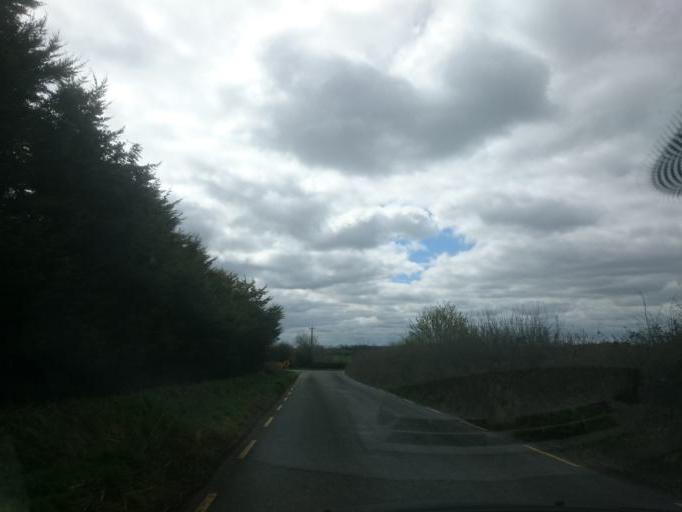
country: IE
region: Leinster
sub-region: Kilkenny
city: Ballyragget
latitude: 52.6726
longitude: -7.3780
